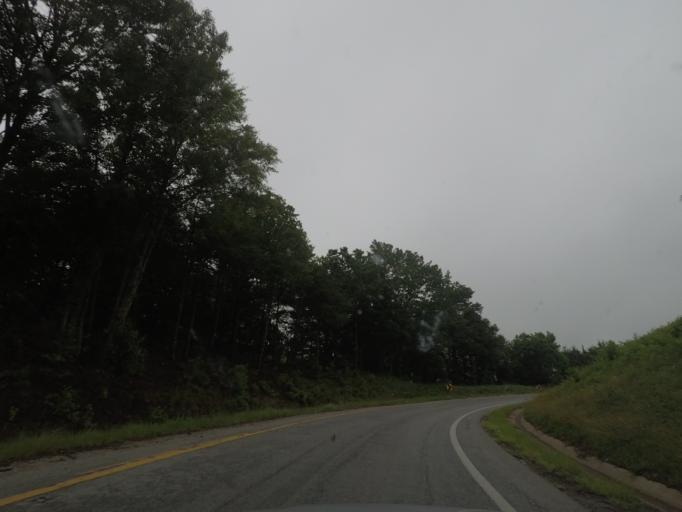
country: US
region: Virginia
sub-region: Charlotte County
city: Charlotte Court House
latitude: 37.0649
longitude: -78.4703
